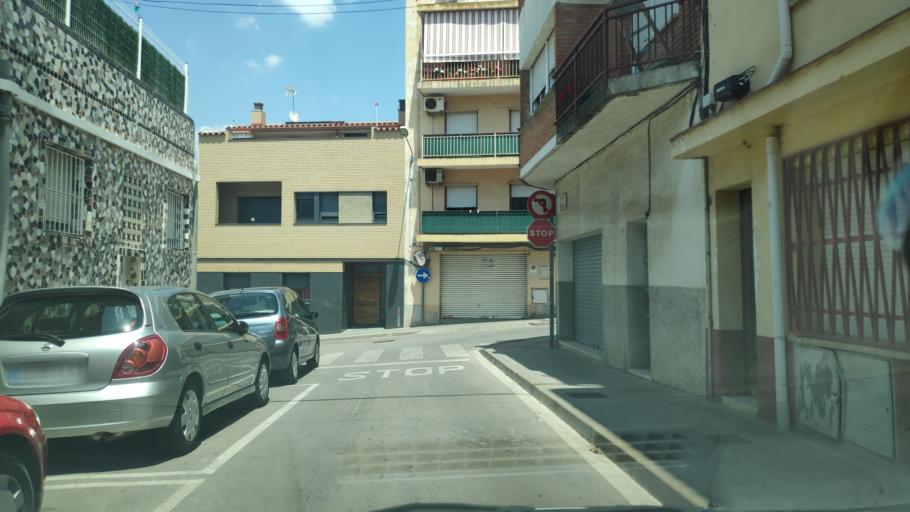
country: ES
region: Catalonia
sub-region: Provincia de Barcelona
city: Les Franqueses del Valles
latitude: 41.6164
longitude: 2.2958
